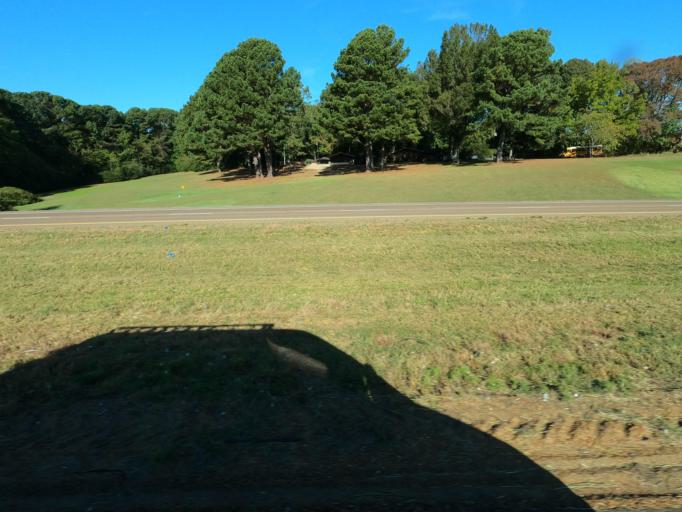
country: US
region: Tennessee
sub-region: Tipton County
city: Munford
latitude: 35.4181
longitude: -89.8229
